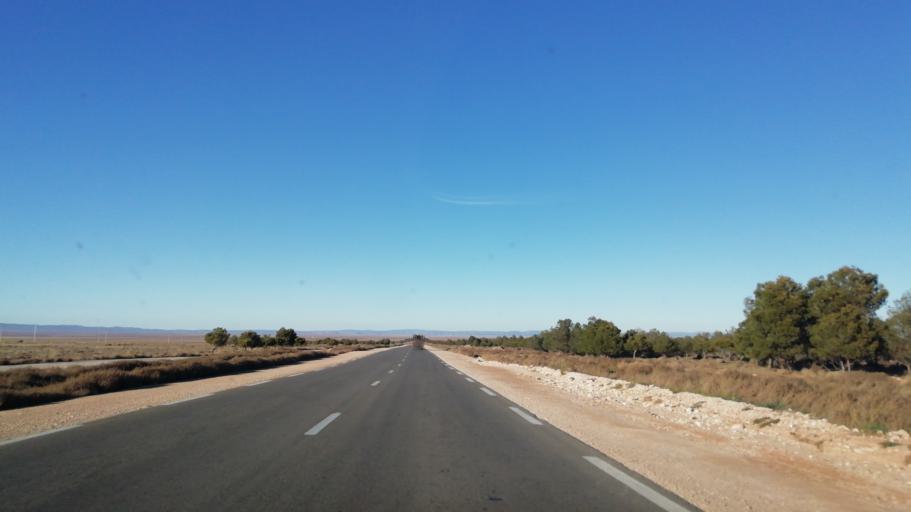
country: DZ
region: Tlemcen
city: Sebdou
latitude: 34.3188
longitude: -1.2630
